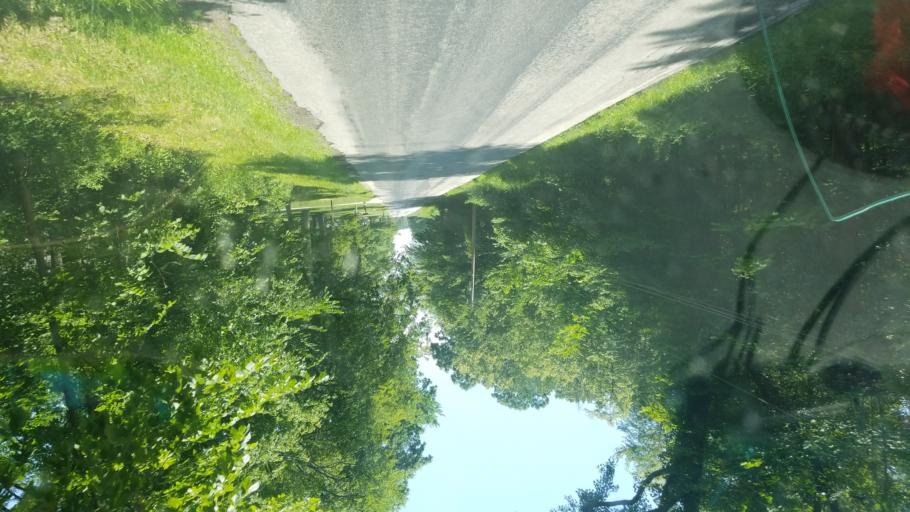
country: US
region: Ohio
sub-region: Richland County
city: Ontario
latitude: 40.8284
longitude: -82.5871
